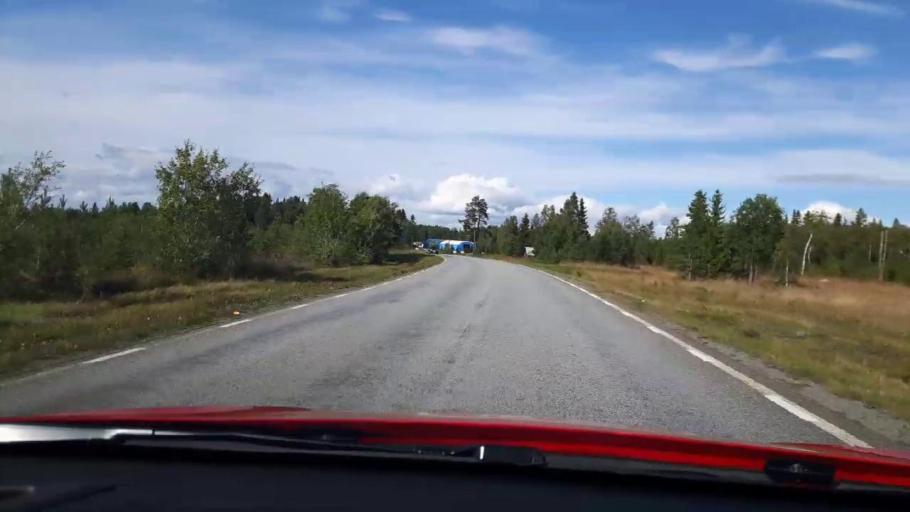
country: SE
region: Jaemtland
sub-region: OEstersunds Kommun
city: Ostersund
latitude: 63.0784
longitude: 14.4448
